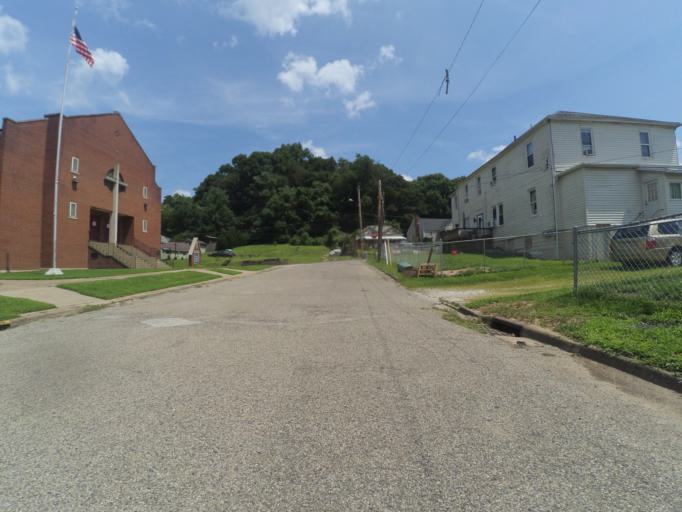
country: US
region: West Virginia
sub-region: Cabell County
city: Huntington
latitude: 38.4174
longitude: -82.4116
